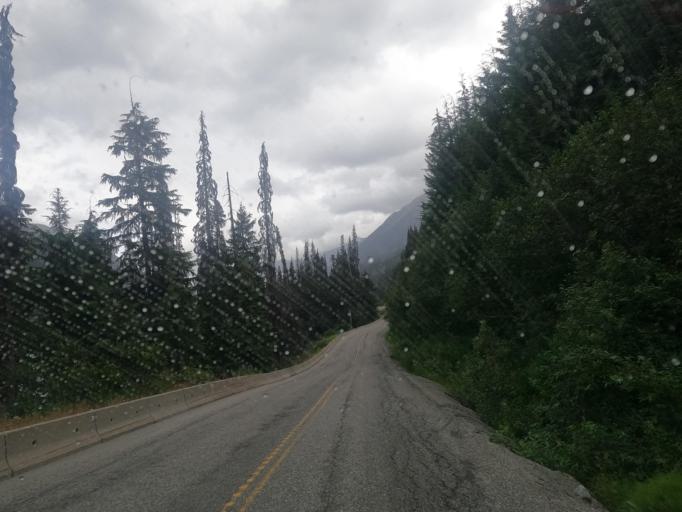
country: CA
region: British Columbia
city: Pemberton
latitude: 50.3947
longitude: -122.3303
